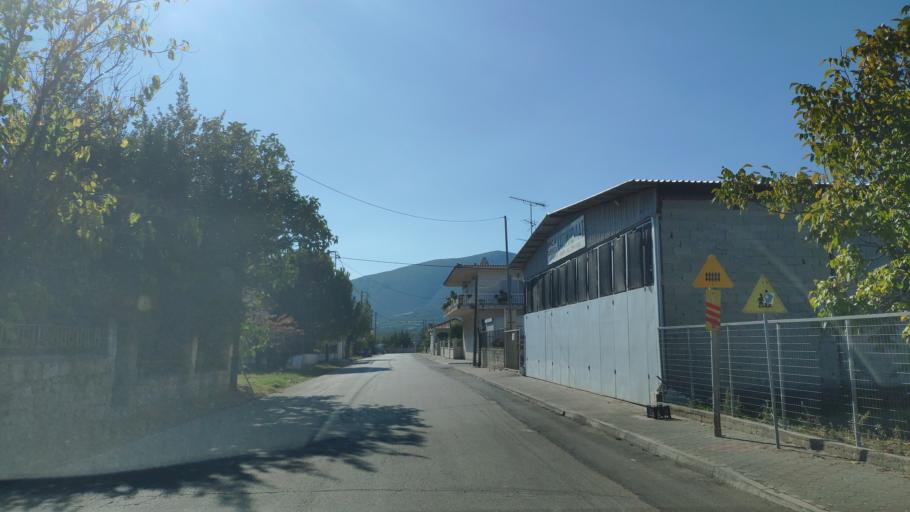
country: GR
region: Peloponnese
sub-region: Nomos Korinthias
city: Khiliomodhi
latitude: 37.8069
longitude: 22.8700
